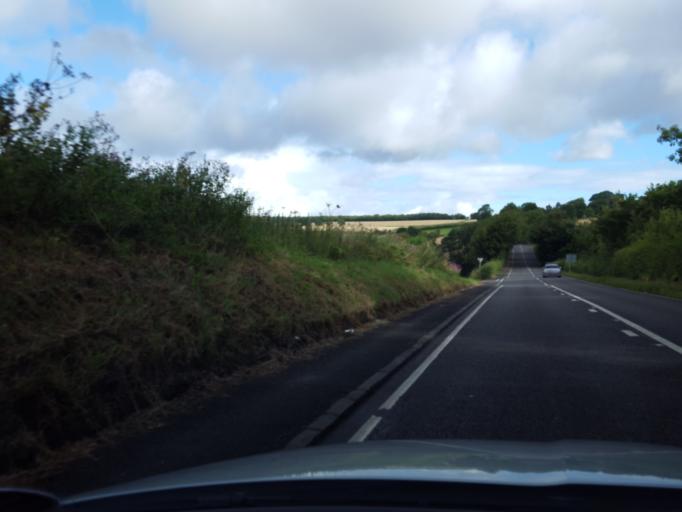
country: GB
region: Scotland
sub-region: West Lothian
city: Linlithgow
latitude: 55.9856
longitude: -3.6138
